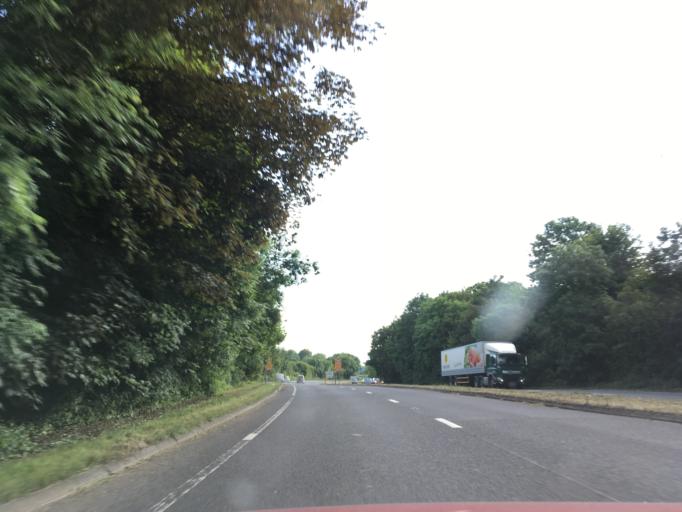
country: GB
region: England
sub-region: Somerset
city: Puriton
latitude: 51.1665
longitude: -2.9845
